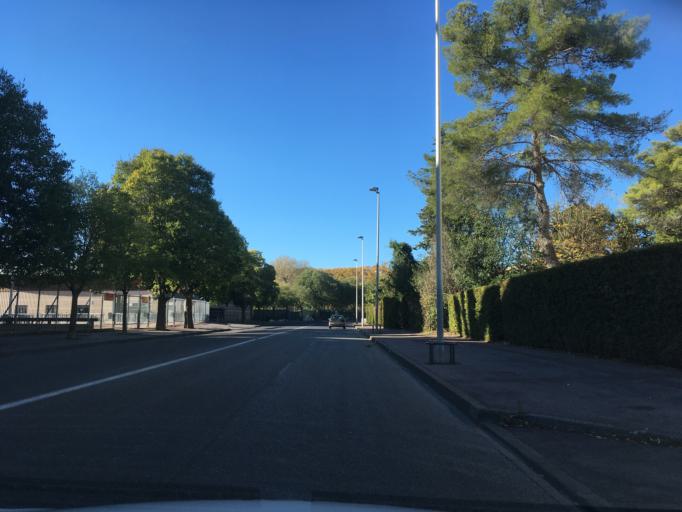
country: FR
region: Languedoc-Roussillon
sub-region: Departement de l'Herault
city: Juvignac
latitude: 43.6229
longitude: 3.8126
